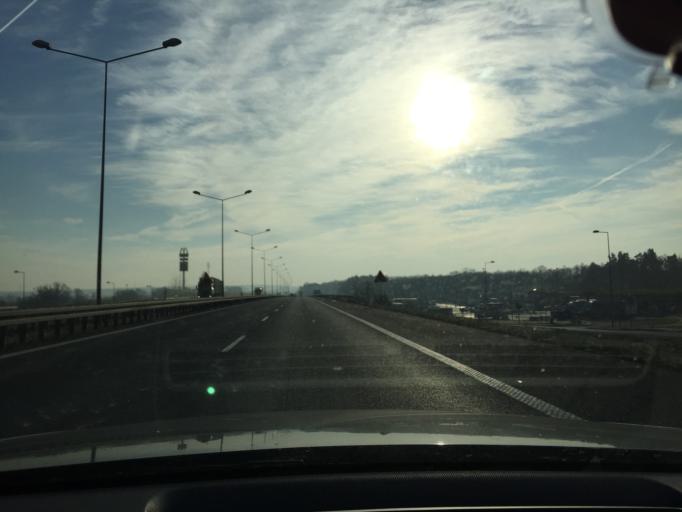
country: PL
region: Silesian Voivodeship
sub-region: Powiat gliwicki
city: Sosnicowice
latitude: 50.3133
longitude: 18.5503
